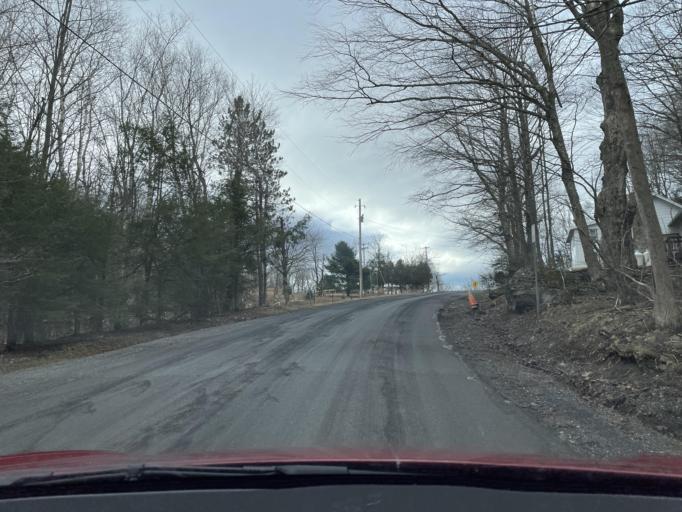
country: US
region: New York
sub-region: Ulster County
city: Woodstock
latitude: 42.0724
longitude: -74.1241
